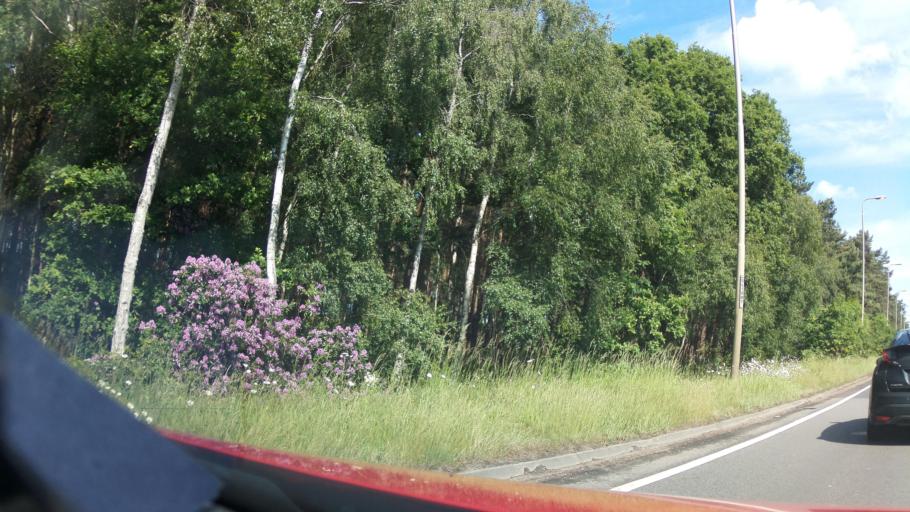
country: GB
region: England
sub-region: Lincolnshire
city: Skellingthorpe
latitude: 53.2099
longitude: -0.6176
